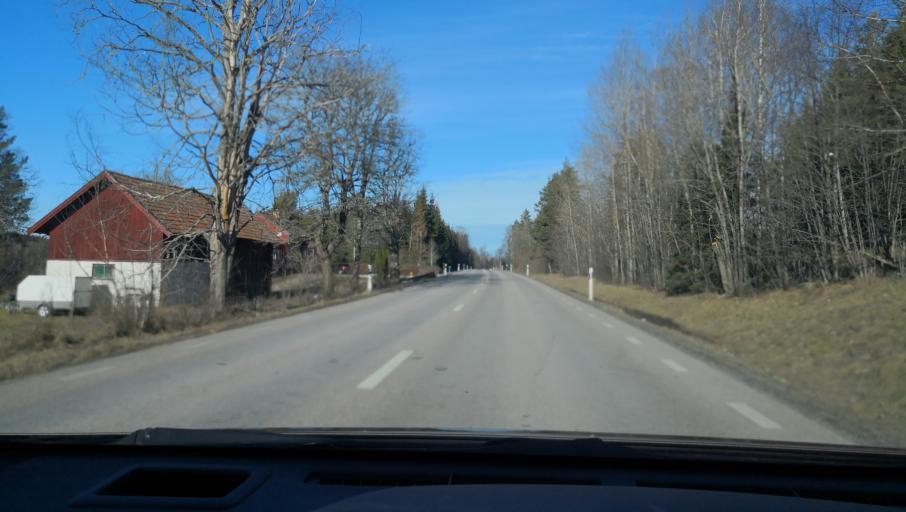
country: SE
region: Uppsala
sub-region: Uppsala Kommun
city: Vattholma
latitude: 60.0793
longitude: 17.7620
